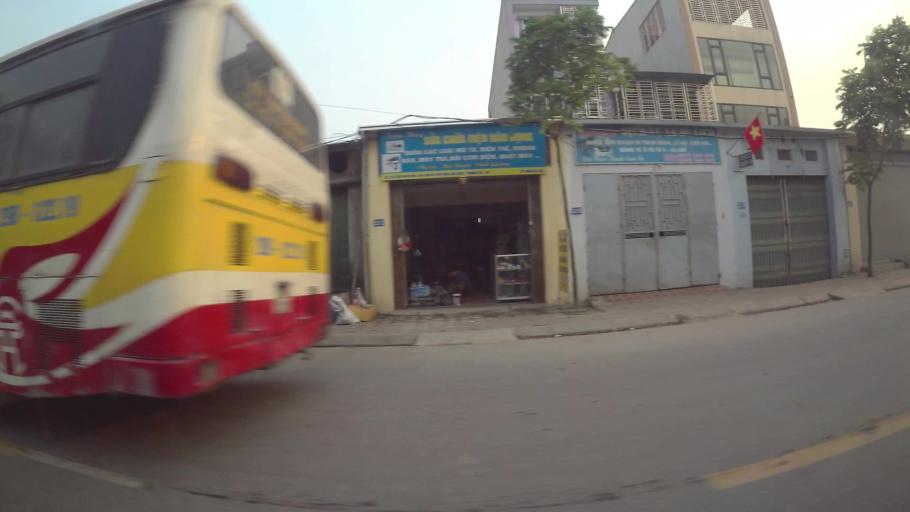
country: VN
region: Ha Noi
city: Thuong Tin
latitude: 20.8689
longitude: 105.8400
